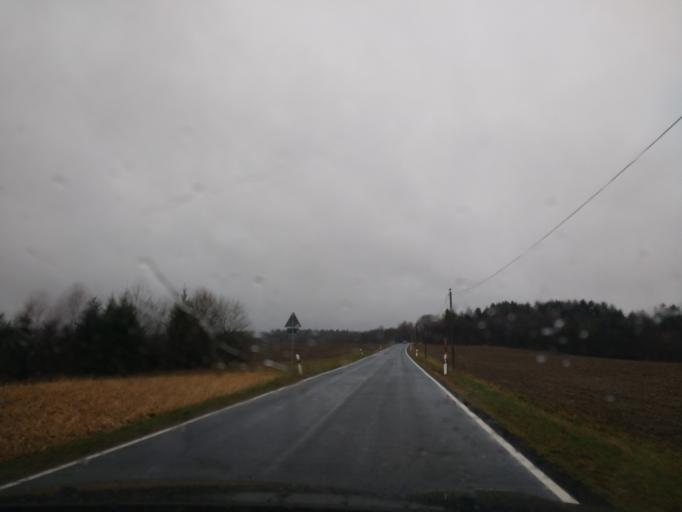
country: DE
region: Rheinland-Pfalz
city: Geisfeld
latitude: 49.6941
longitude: 6.9460
